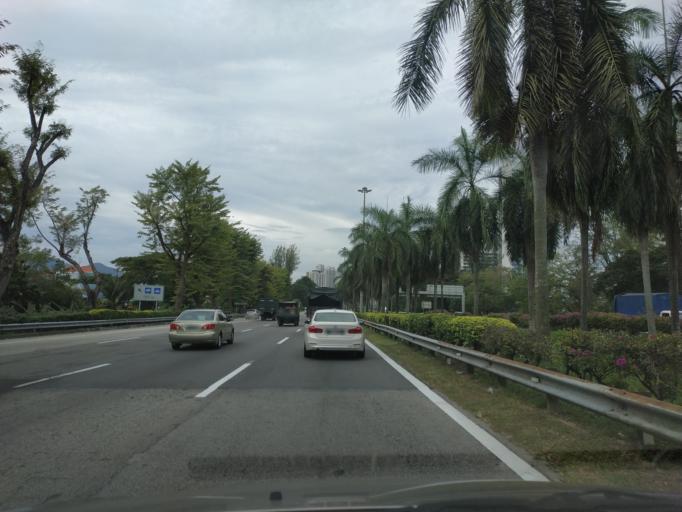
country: MY
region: Penang
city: George Town
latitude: 5.3647
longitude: 100.3142
